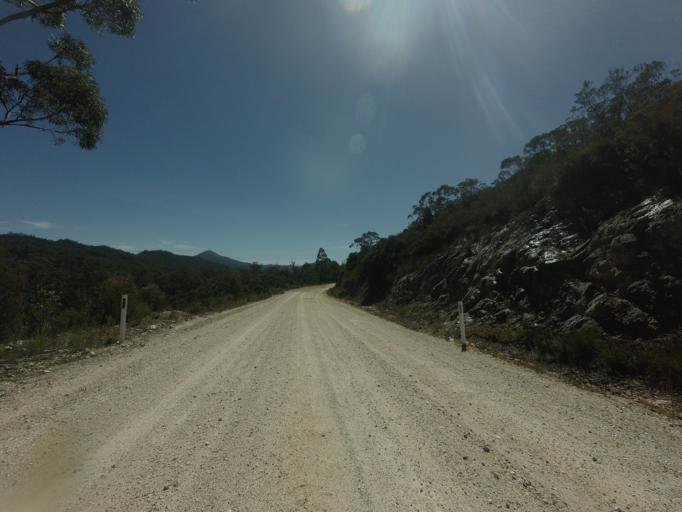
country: AU
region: Tasmania
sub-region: Huon Valley
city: Geeveston
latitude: -42.9301
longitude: 146.3414
